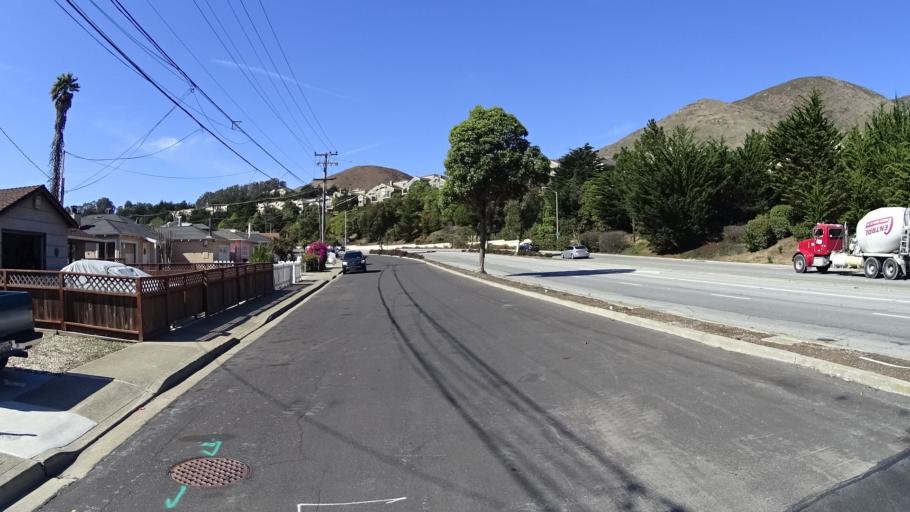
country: US
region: California
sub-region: San Mateo County
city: South San Francisco
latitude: 37.6693
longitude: -122.4184
